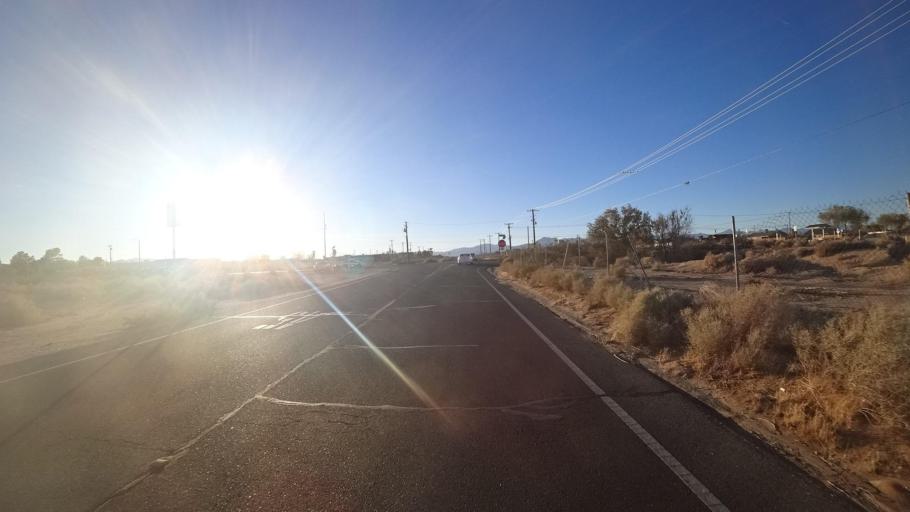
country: US
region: California
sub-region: Kern County
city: Ridgecrest
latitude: 35.6075
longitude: -117.6874
